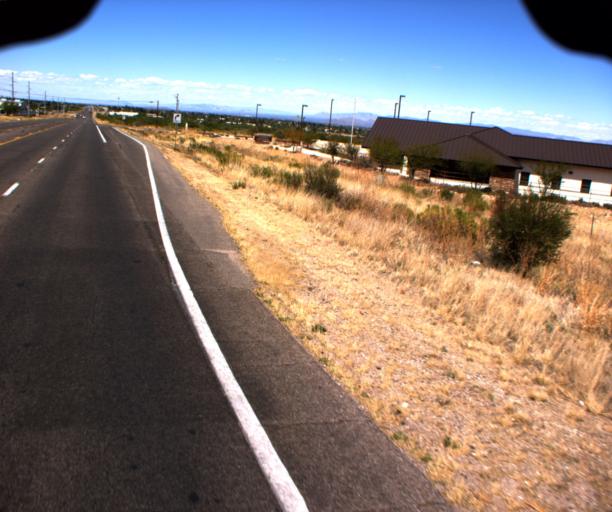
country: US
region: Arizona
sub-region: Cochise County
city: Sierra Vista Southeast
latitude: 31.4579
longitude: -110.2573
